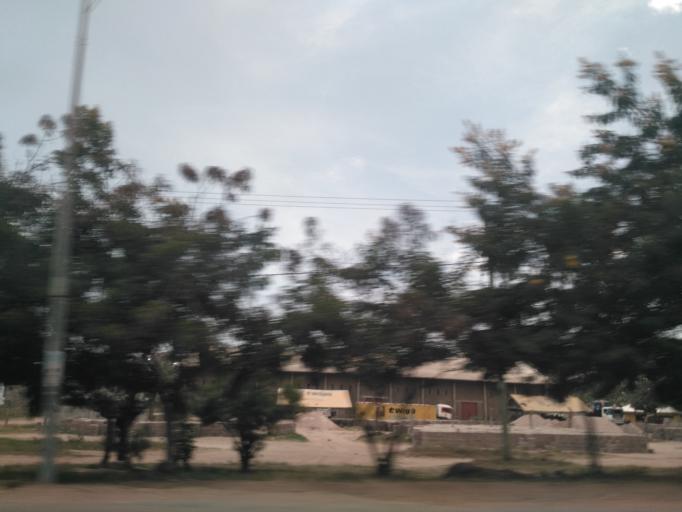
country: TZ
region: Mwanza
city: Mwanza
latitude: -2.5663
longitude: 32.9181
